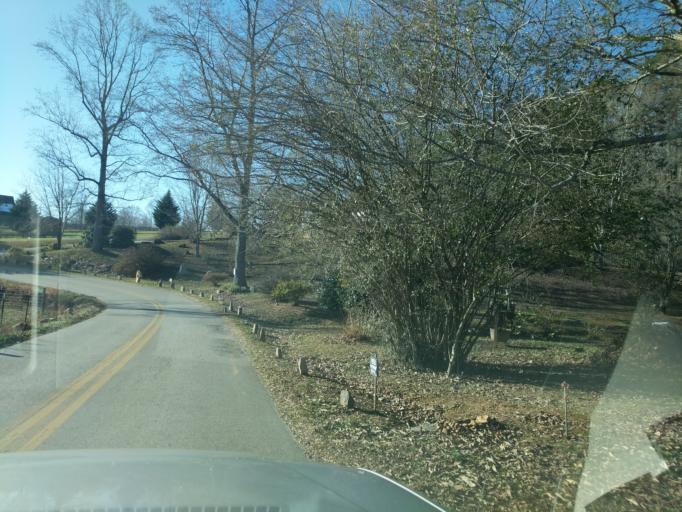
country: US
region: Georgia
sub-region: Towns County
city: Hiawassee
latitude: 34.9429
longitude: -83.7323
